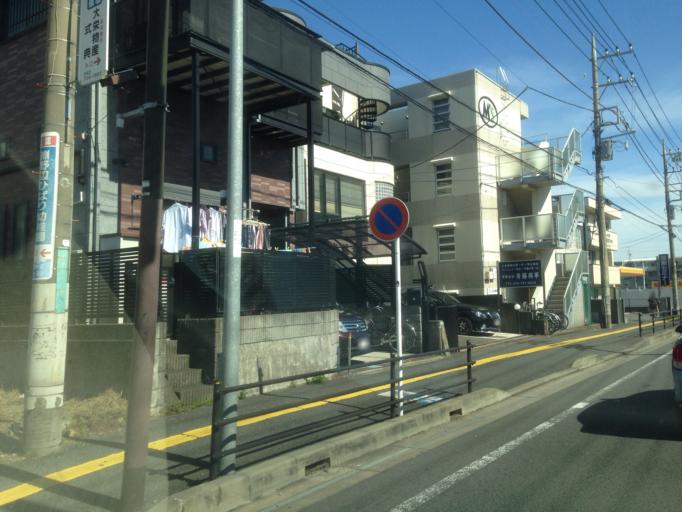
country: JP
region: Tokyo
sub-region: Machida-shi
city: Machida
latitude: 35.5696
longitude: 139.4007
